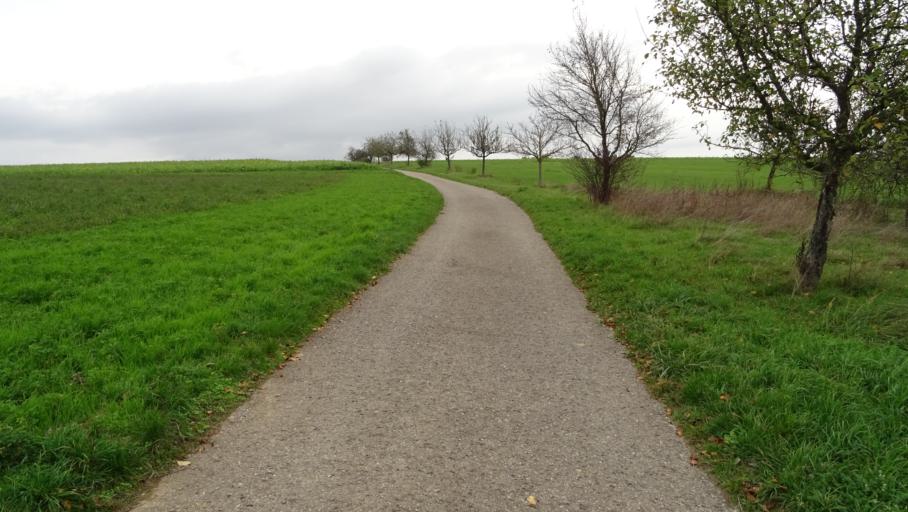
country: DE
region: Baden-Wuerttemberg
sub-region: Karlsruhe Region
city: Mosbach
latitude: 49.3637
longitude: 9.1214
